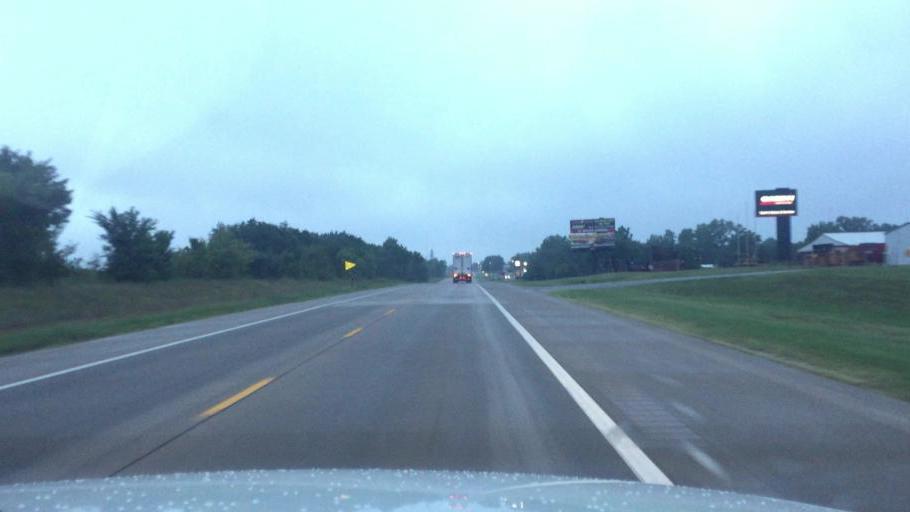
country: US
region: Kansas
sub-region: Neosho County
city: Chanute
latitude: 37.4980
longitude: -95.4705
